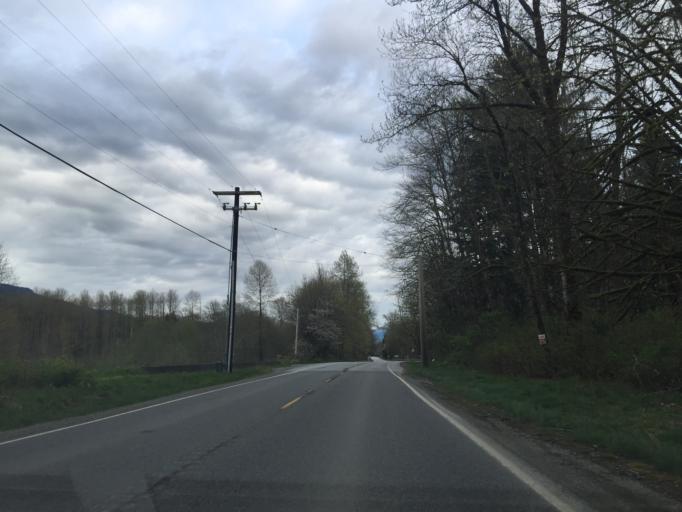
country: US
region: Washington
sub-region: Snohomish County
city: Darrington
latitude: 48.2770
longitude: -121.8107
